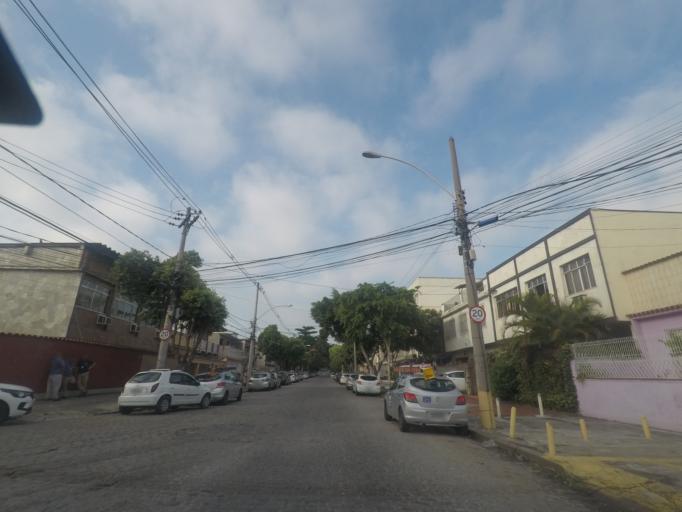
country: BR
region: Rio de Janeiro
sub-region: Duque De Caxias
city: Duque de Caxias
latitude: -22.8375
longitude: -43.2644
